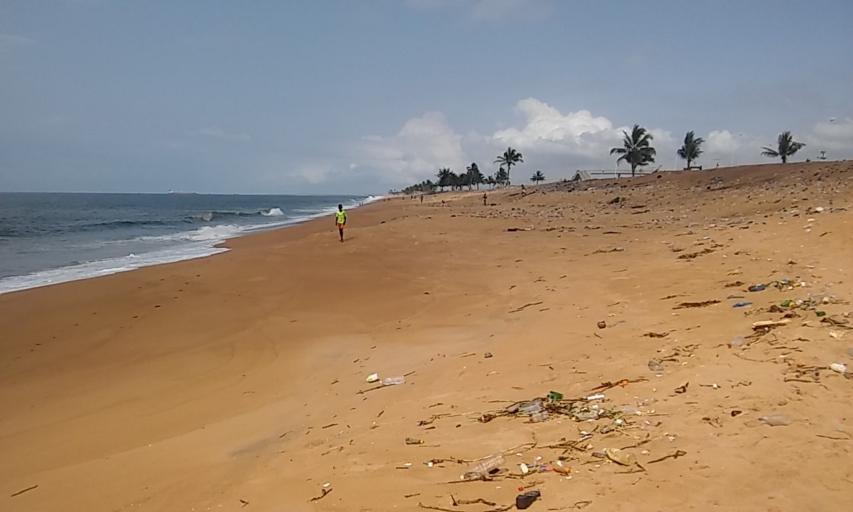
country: CI
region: Lagunes
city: Bingerville
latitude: 5.2388
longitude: -3.8992
